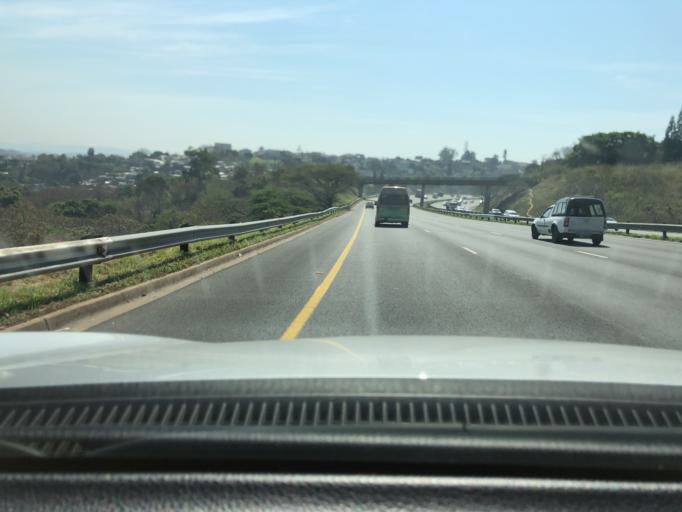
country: ZA
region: KwaZulu-Natal
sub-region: eThekwini Metropolitan Municipality
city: Berea
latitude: -29.8248
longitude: 30.9671
